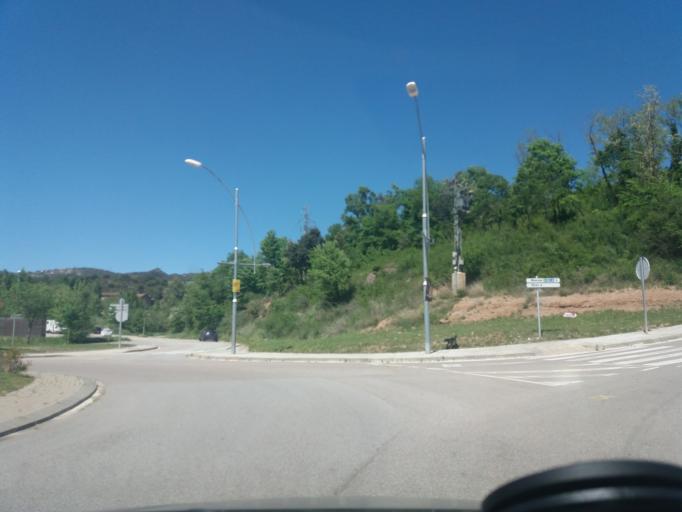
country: ES
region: Catalonia
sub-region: Provincia de Barcelona
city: Avia
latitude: 42.0718
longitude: 1.8702
